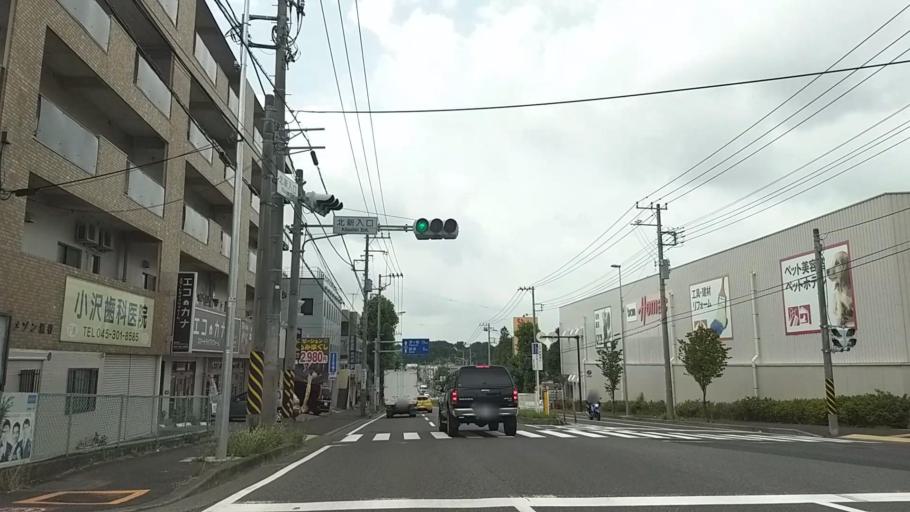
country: JP
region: Kanagawa
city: Minami-rinkan
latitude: 35.4580
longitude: 139.4798
